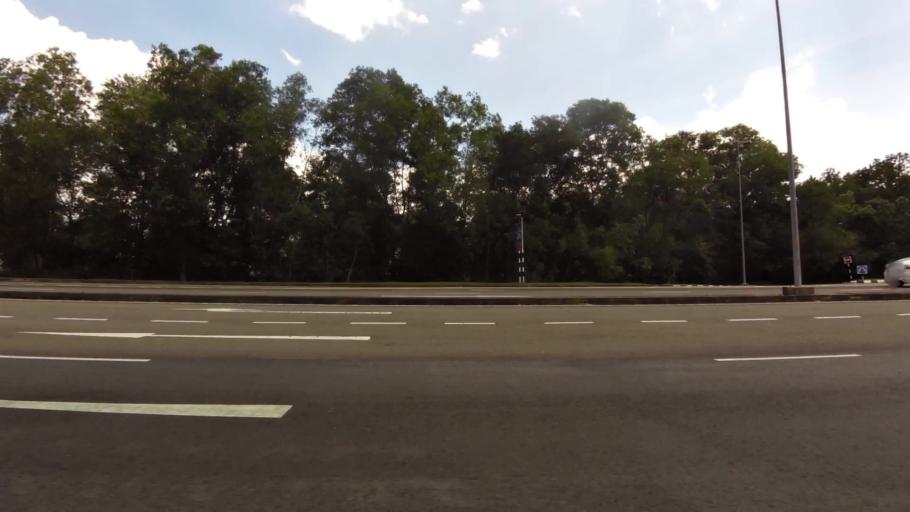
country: BN
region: Brunei and Muara
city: Bandar Seri Begawan
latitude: 4.9478
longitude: 114.9653
